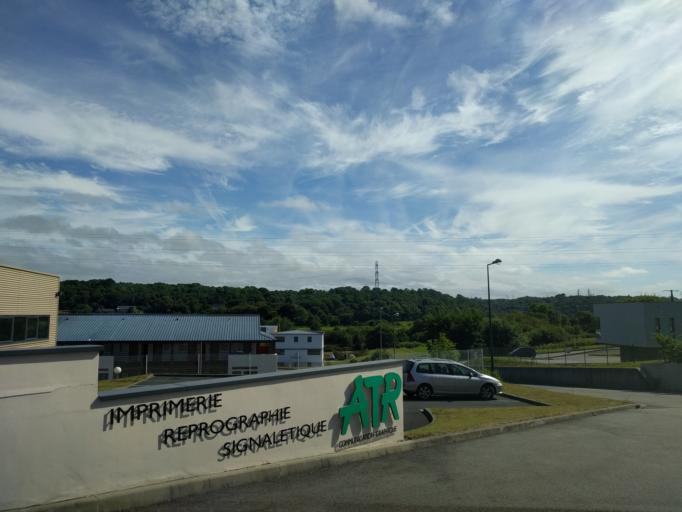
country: FR
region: Brittany
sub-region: Departement du Finistere
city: Quimper
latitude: 48.0109
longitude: -4.0742
